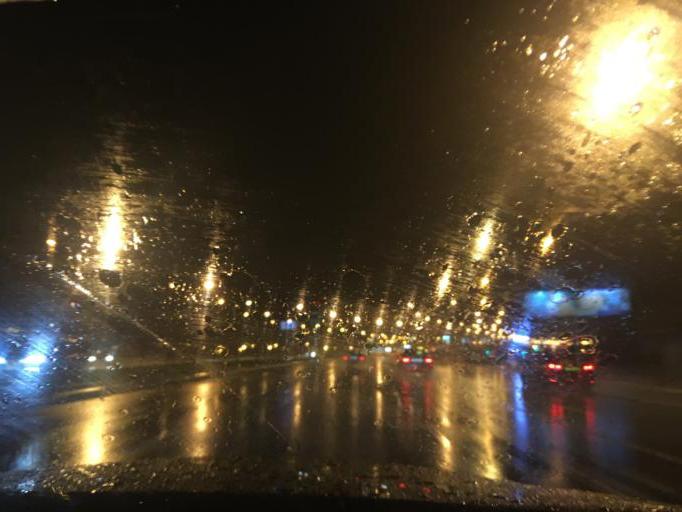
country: BY
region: Minsk
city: Novoye Medvezhino
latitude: 53.8801
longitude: 27.4997
